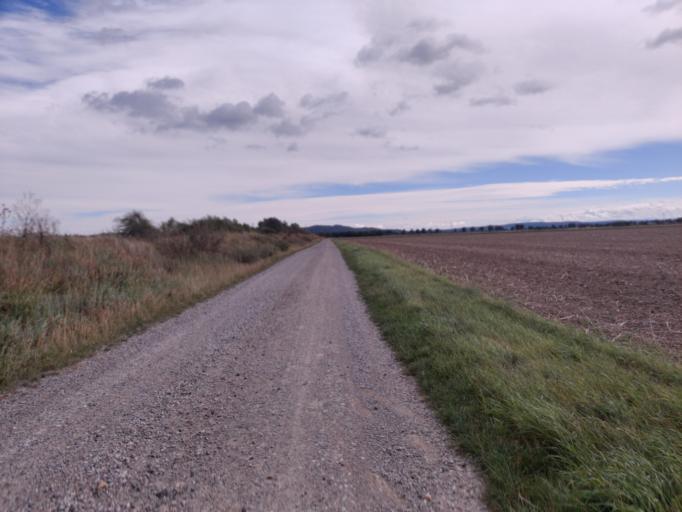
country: DE
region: Lower Saxony
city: Alt Wallmoden
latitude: 52.0267
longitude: 10.3148
